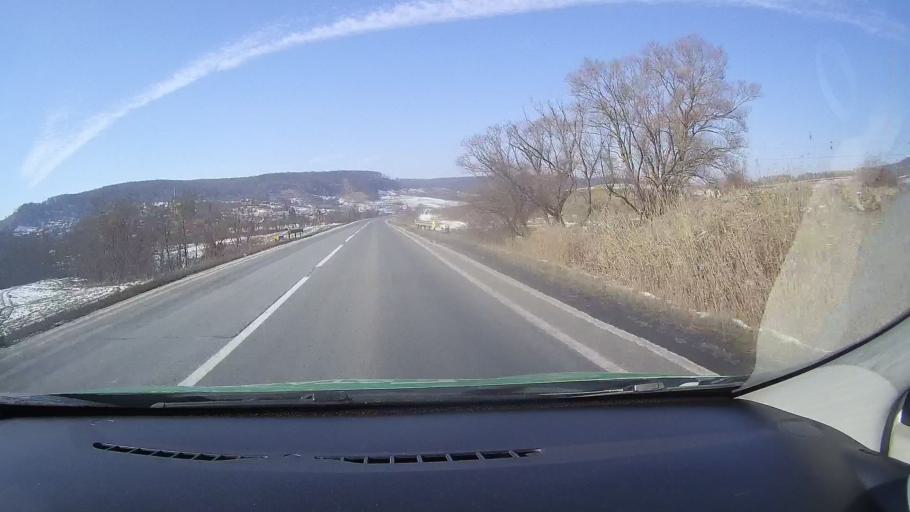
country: RO
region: Brasov
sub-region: Comuna Bunesti
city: Bunesti
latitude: 46.1214
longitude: 25.0264
